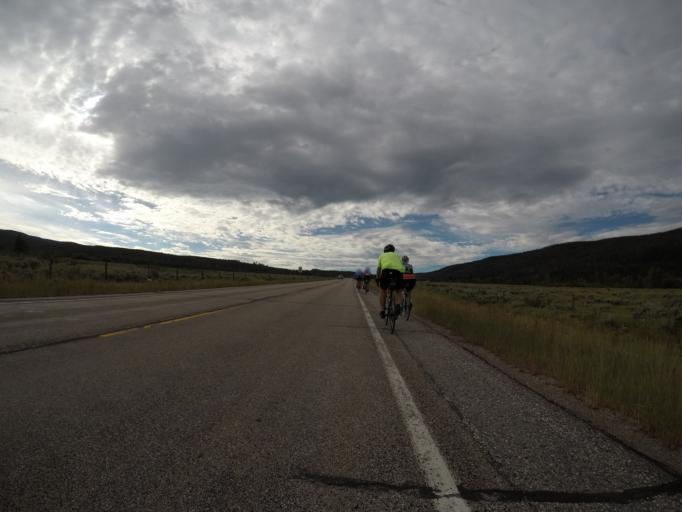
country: US
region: Wyoming
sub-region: Carbon County
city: Saratoga
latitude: 41.3521
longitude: -106.5340
